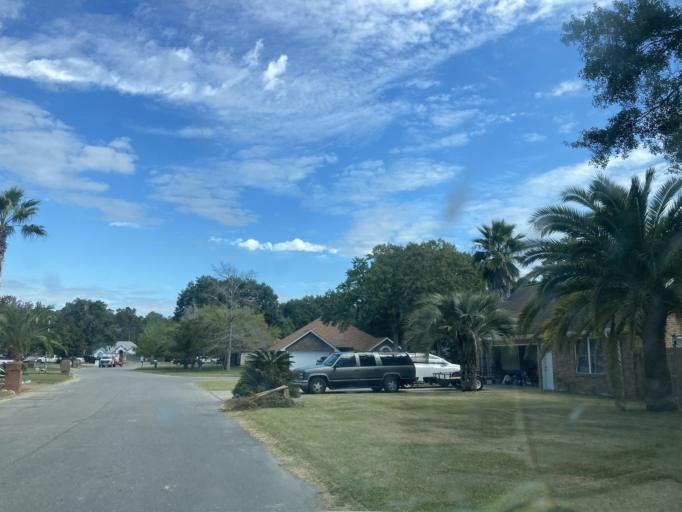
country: US
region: Mississippi
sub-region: Jackson County
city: Saint Martin
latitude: 30.4382
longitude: -88.8560
